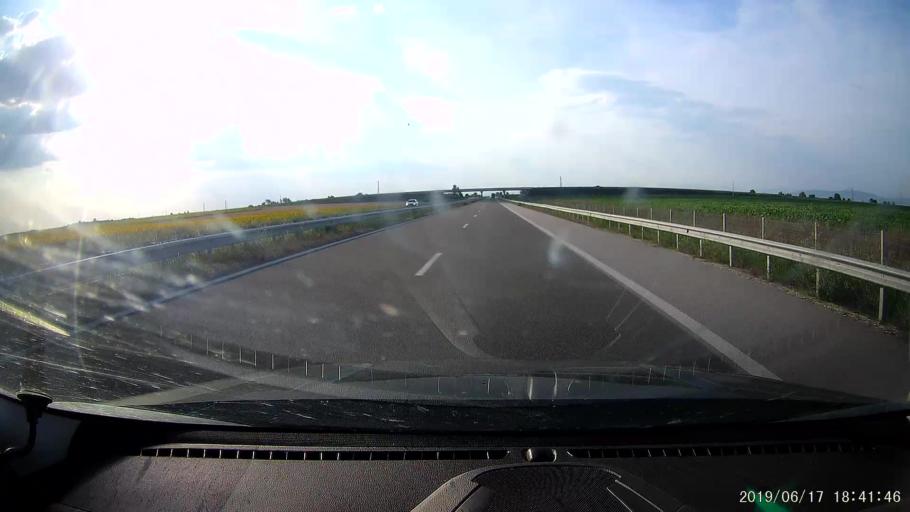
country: BG
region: Stara Zagora
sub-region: Obshtina Chirpan
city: Chirpan
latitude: 42.1786
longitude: 25.2495
